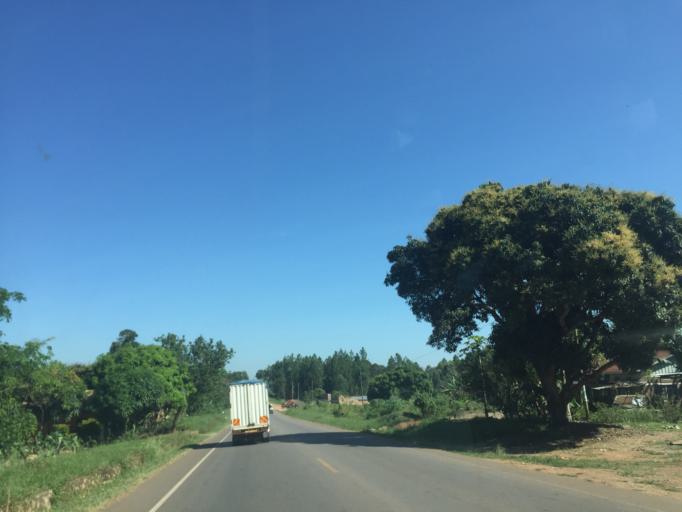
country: UG
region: Central Region
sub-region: Luwero District
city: Wobulenzi
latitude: 0.7762
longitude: 32.5113
